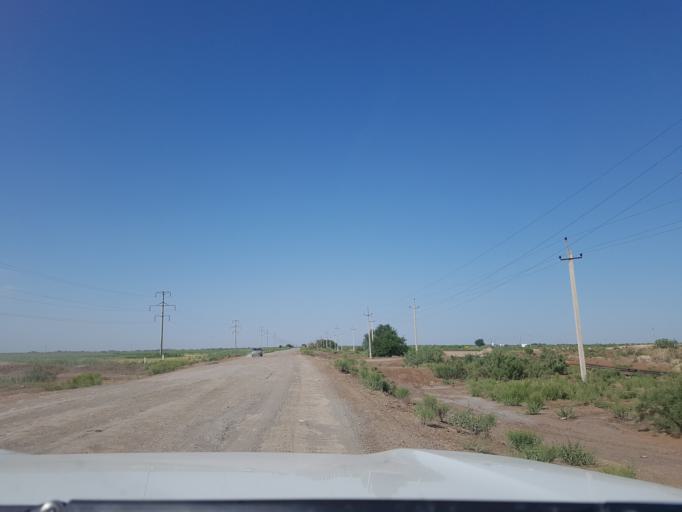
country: TM
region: Dasoguz
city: Koeneuergench
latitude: 42.1393
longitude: 58.9585
